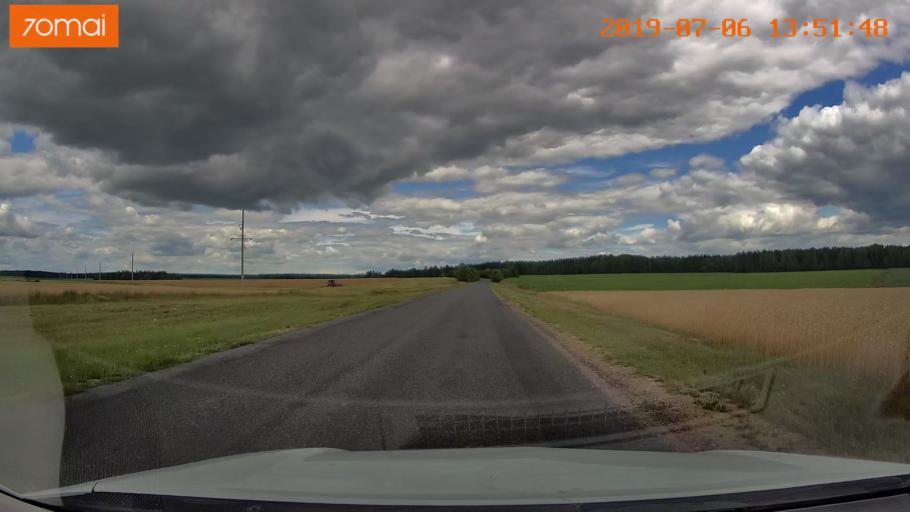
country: BY
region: Minsk
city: Ivyanyets
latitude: 53.7125
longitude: 26.8289
